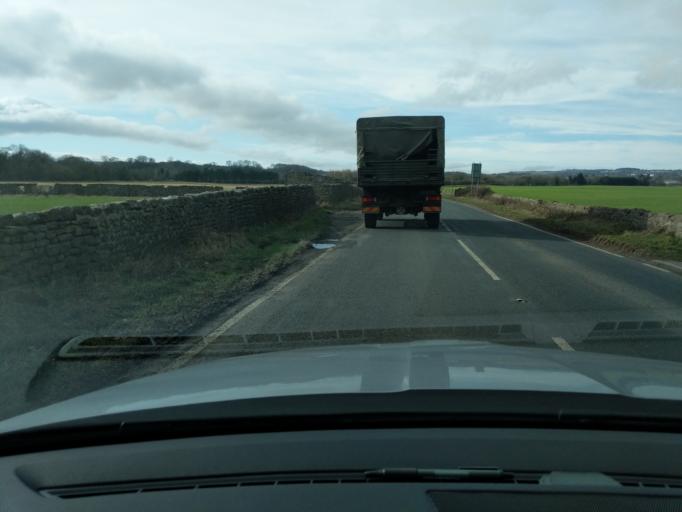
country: GB
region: England
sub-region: North Yorkshire
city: Catterick
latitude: 54.3941
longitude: -1.6759
